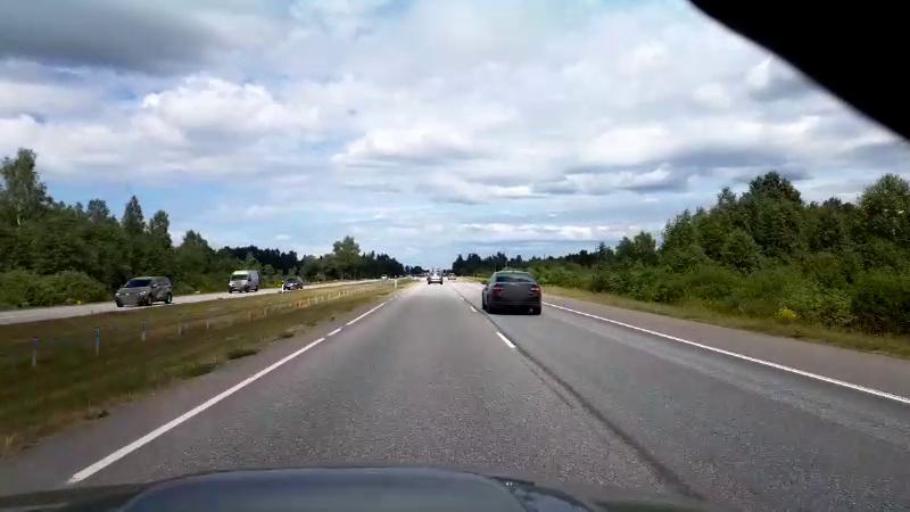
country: EE
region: Harju
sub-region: Saue linn
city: Saue
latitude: 59.2920
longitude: 24.5447
